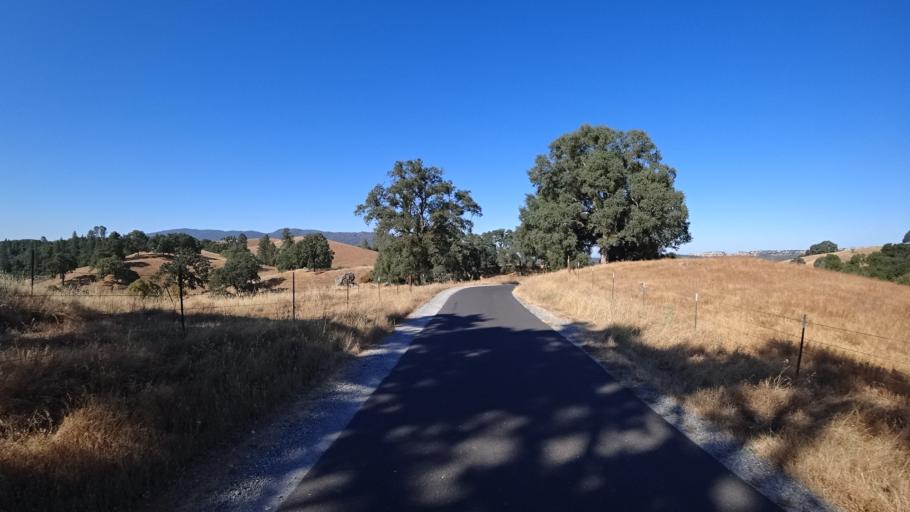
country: US
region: California
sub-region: Calaveras County
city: San Andreas
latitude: 38.2218
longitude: -120.6833
